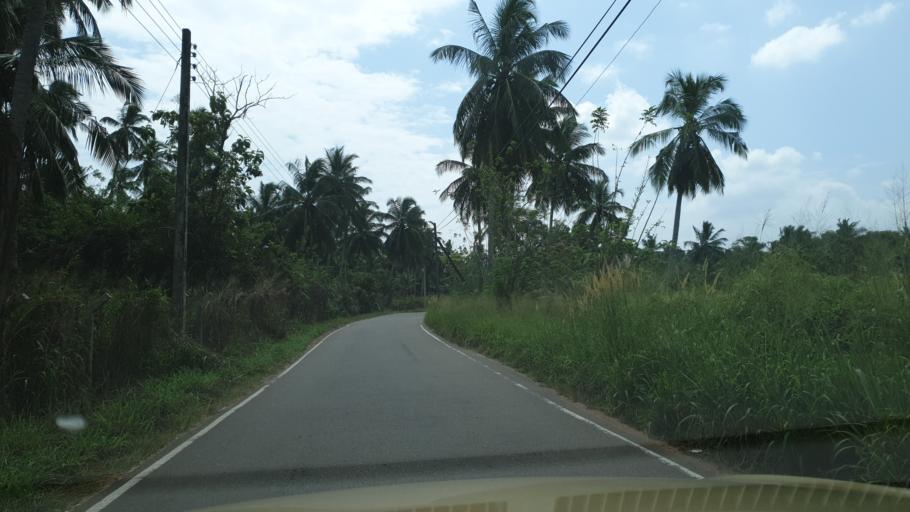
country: LK
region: North Western
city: Kuliyapitiya
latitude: 7.3582
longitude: 79.9675
